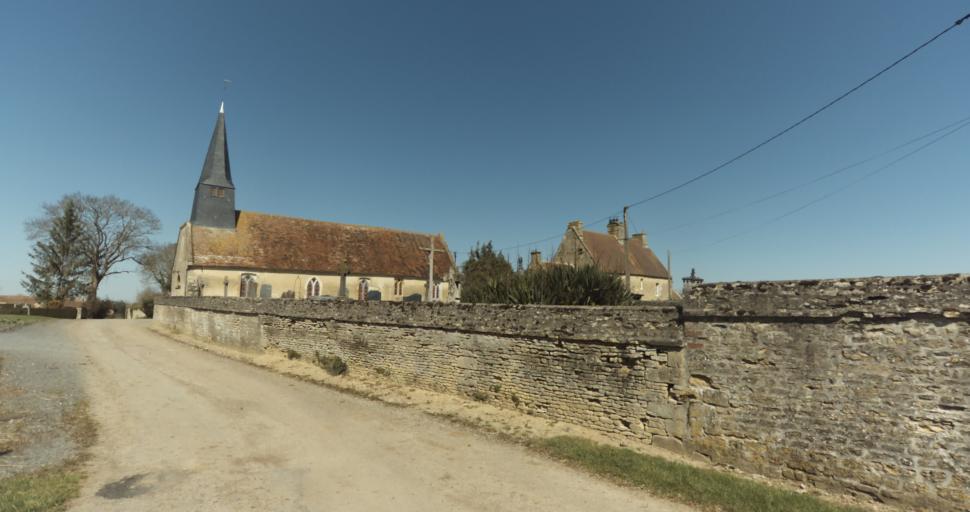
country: FR
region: Lower Normandy
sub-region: Departement du Calvados
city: Saint-Pierre-sur-Dives
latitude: 48.9754
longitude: -0.0064
